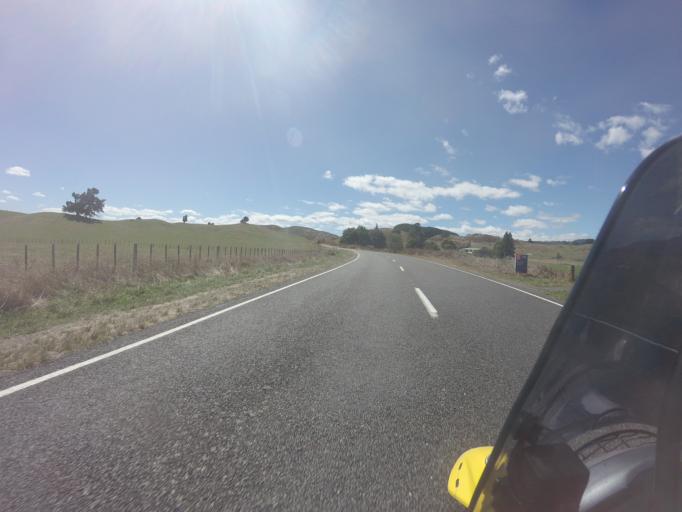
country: NZ
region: Bay of Plenty
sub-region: Whakatane District
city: Murupara
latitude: -38.3196
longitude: 176.7976
